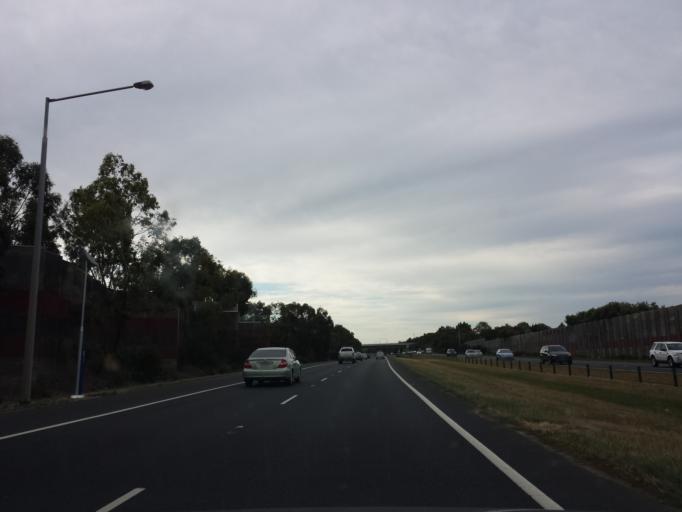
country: AU
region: Victoria
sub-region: Casey
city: Narre Warren
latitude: -38.0098
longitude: 145.3011
